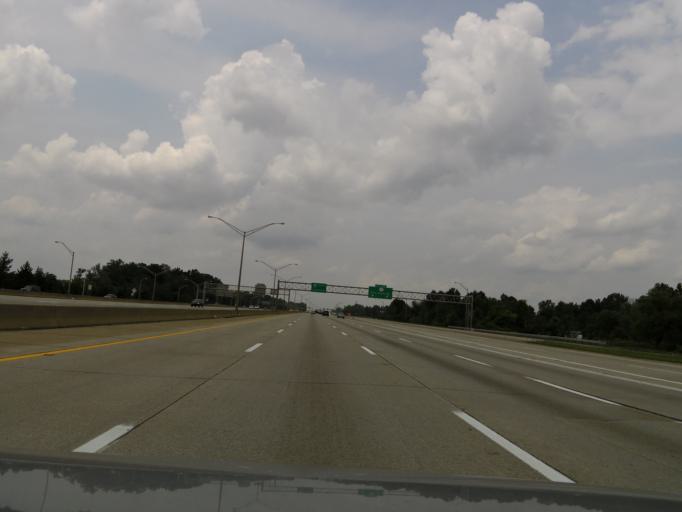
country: US
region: Kentucky
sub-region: Jefferson County
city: Heritage Creek
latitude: 38.1384
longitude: -85.7075
